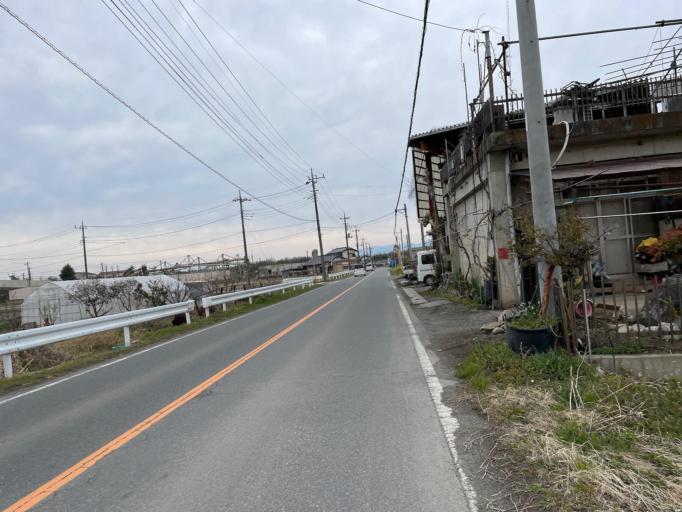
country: JP
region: Gunma
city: Fujioka
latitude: 36.2279
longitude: 139.0998
